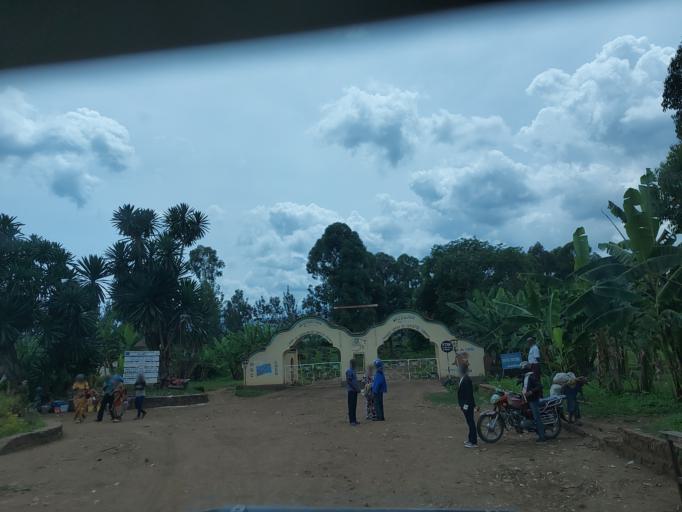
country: CD
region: South Kivu
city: Bukavu
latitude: -2.2441
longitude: 28.8141
